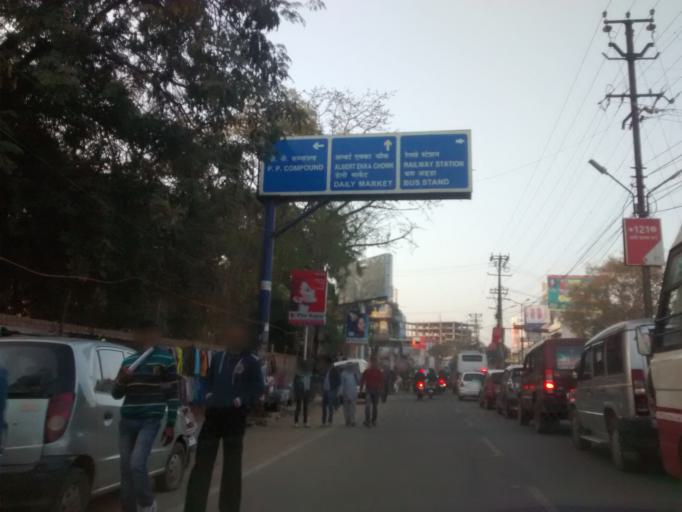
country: IN
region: Jharkhand
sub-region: Ranchi
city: Ranchi
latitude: 23.3529
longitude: 85.3247
